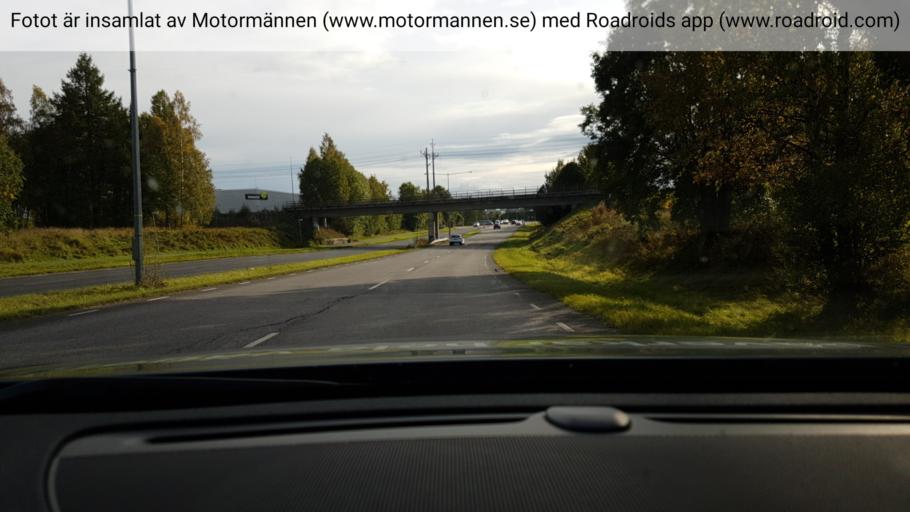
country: SE
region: Norrbotten
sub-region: Lulea Kommun
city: Lulea
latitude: 65.6059
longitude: 22.1380
